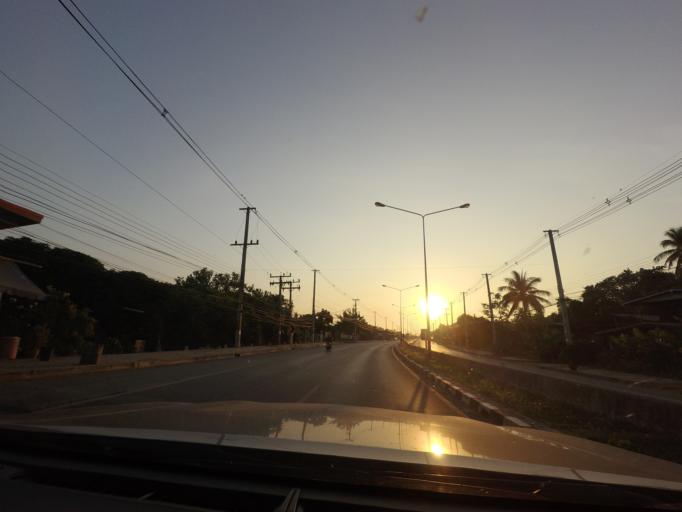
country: TH
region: Sukhothai
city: Si Samrong
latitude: 17.1133
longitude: 99.8498
